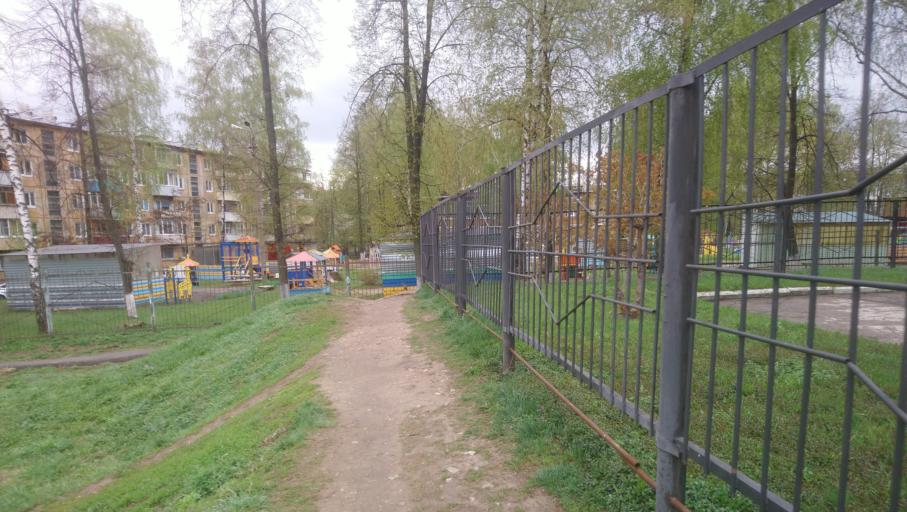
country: RU
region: Tula
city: Tula
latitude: 54.1939
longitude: 37.6739
